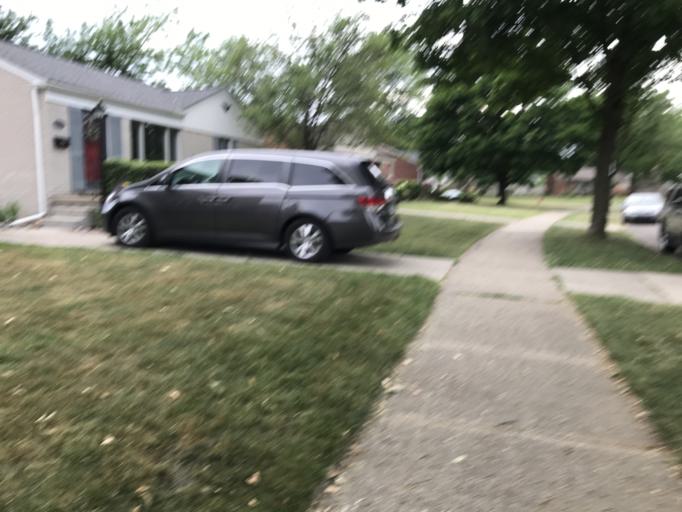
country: US
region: Michigan
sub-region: Oakland County
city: Farmington
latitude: 42.4664
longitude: -83.3610
